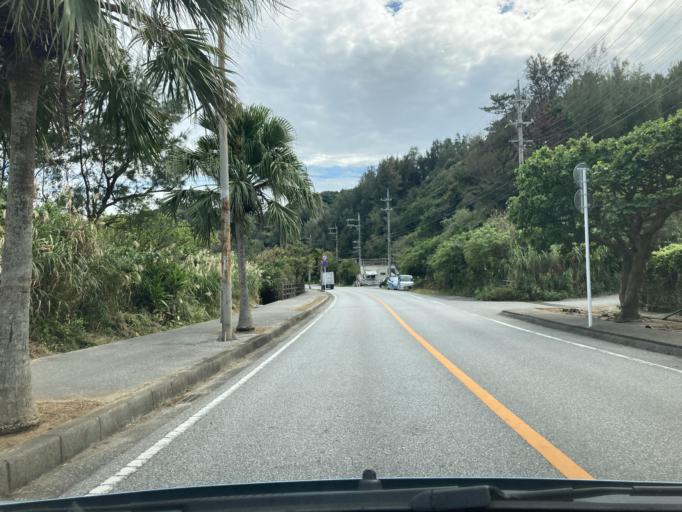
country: JP
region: Okinawa
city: Ishikawa
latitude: 26.4367
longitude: 127.7807
